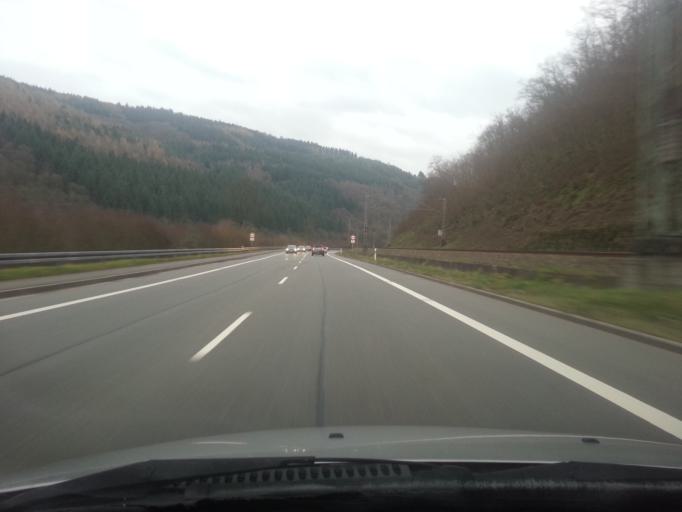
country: DE
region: Hesse
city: Hirschhorn
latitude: 49.4298
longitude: 8.8927
